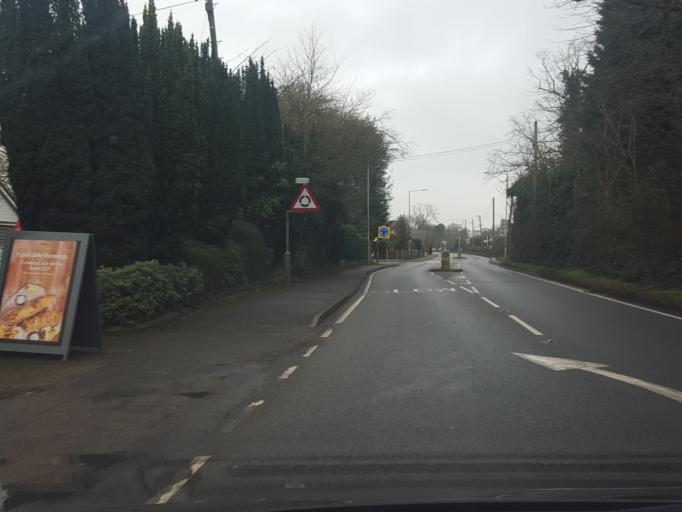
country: GB
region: England
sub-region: Essex
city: Great Horkesley
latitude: 51.9375
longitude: 0.8757
